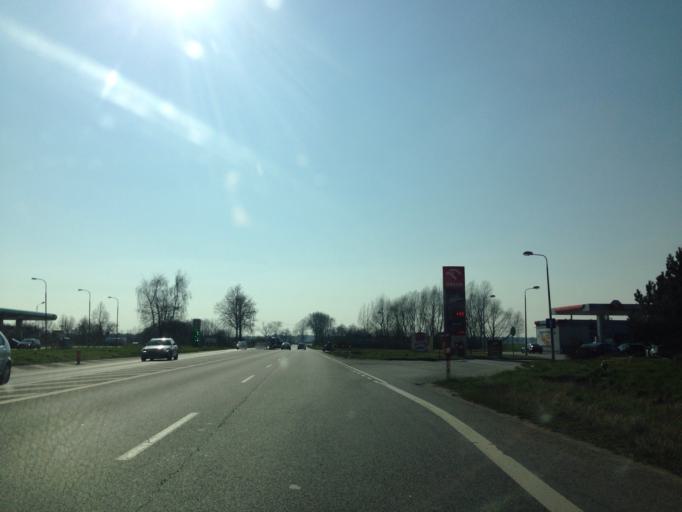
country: PL
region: Lower Silesian Voivodeship
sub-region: Powiat olesnicki
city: Dobroszyce
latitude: 51.1998
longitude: 17.3157
